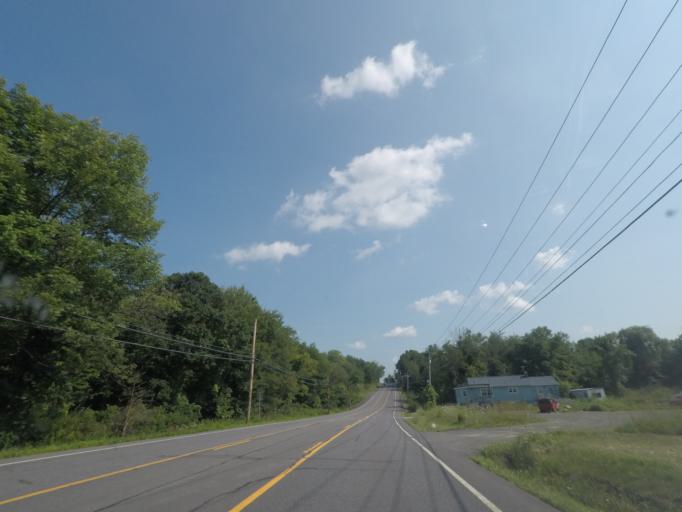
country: US
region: New York
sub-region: Rensselaer County
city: Nassau
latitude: 42.5367
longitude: -73.6610
